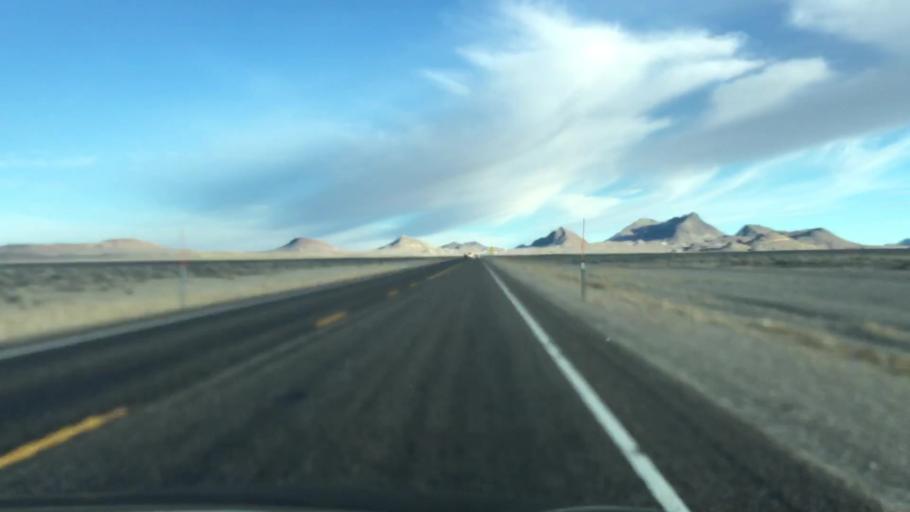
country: US
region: Nevada
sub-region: Nye County
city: Tonopah
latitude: 38.0951
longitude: -117.3131
